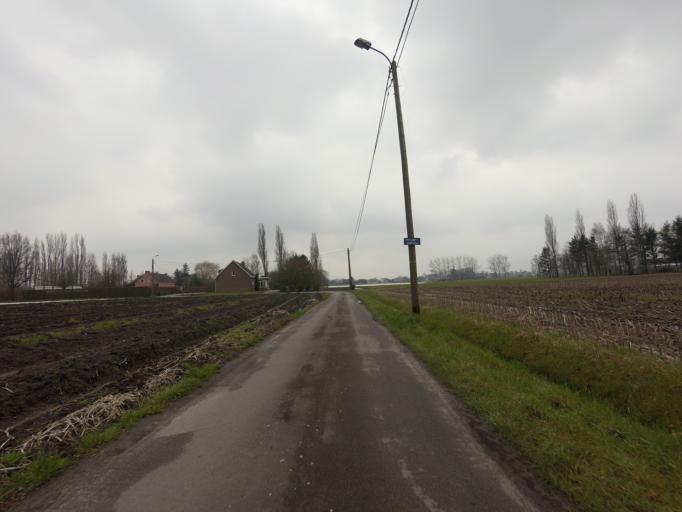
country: BE
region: Flanders
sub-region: Provincie Antwerpen
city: Putte
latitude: 51.0683
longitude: 4.5992
